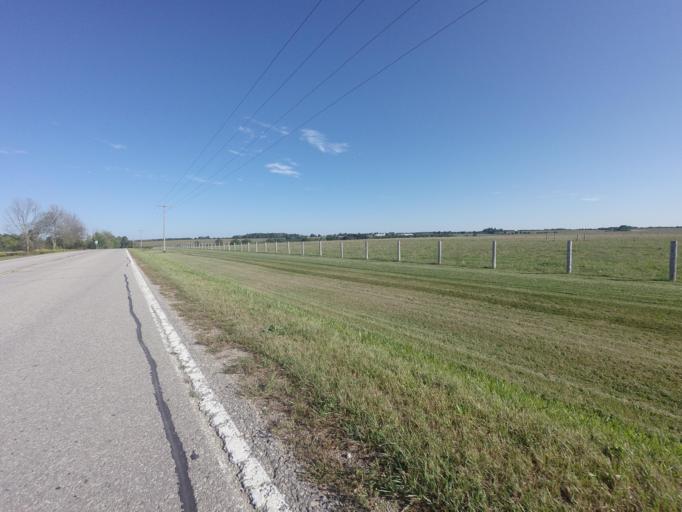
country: CA
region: Ontario
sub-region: Wellington County
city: Guelph
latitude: 43.6479
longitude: -80.4119
